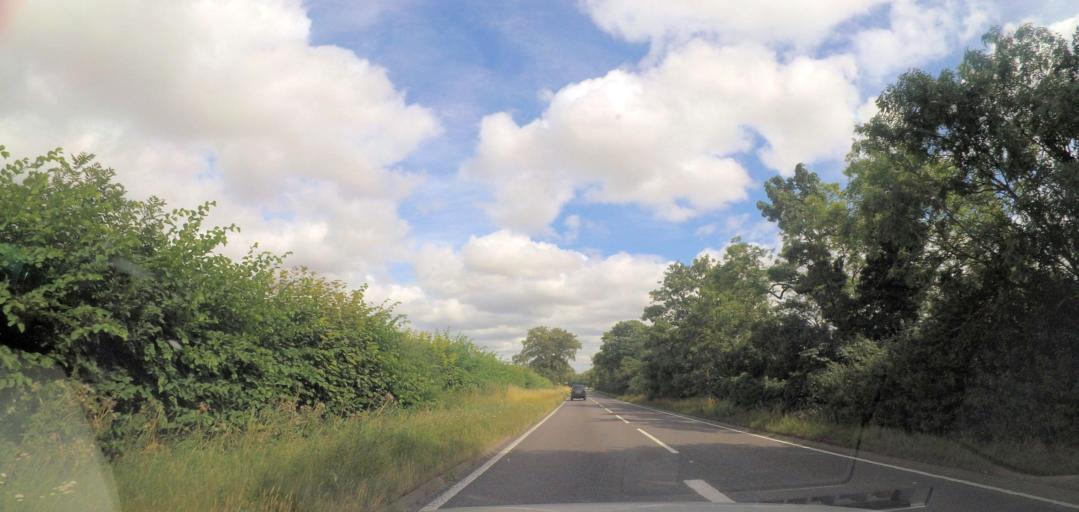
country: GB
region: England
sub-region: Hertfordshire
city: Royston
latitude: 52.0496
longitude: 0.0072
